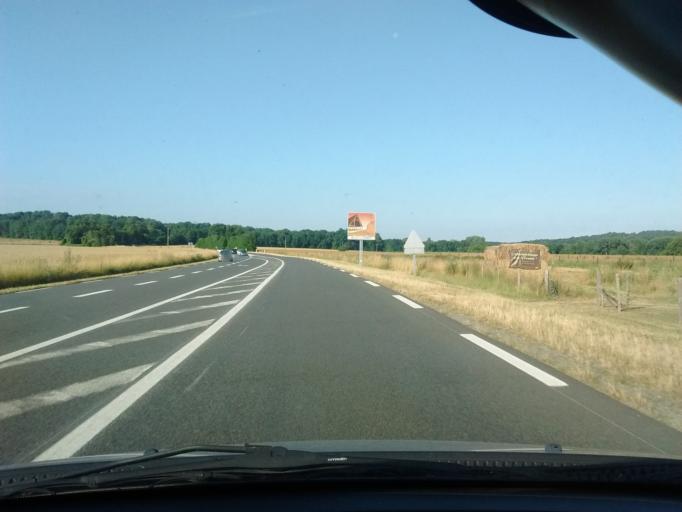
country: FR
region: Ile-de-France
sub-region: Departement de l'Essonne
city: Moigny-sur-Ecole
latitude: 48.4334
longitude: 2.4729
